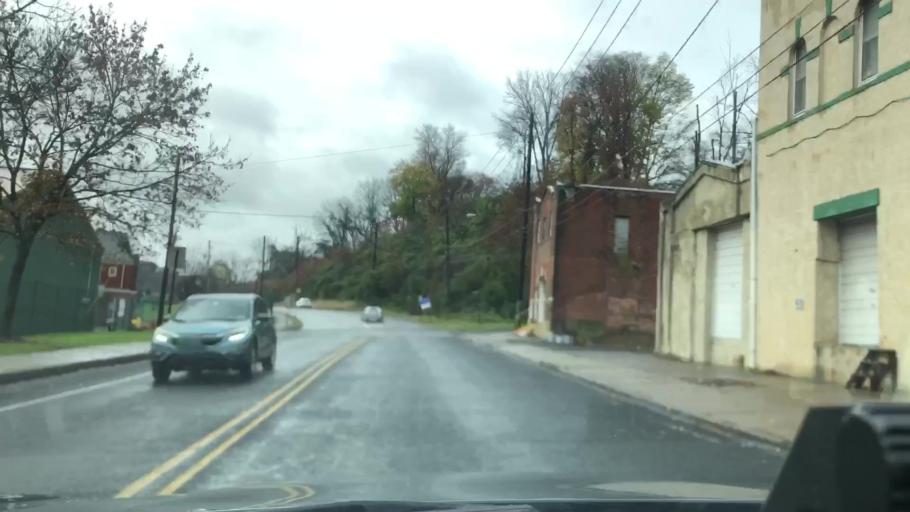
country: US
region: Pennsylvania
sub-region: Lehigh County
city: Allentown
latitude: 40.5959
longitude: -75.4803
